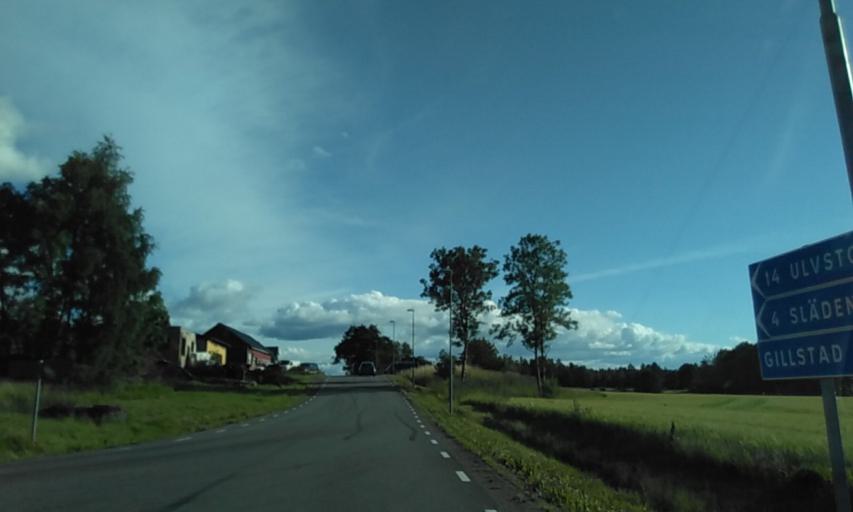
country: SE
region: Vaestra Goetaland
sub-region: Vara Kommun
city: Vara
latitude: 58.4060
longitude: 12.9156
